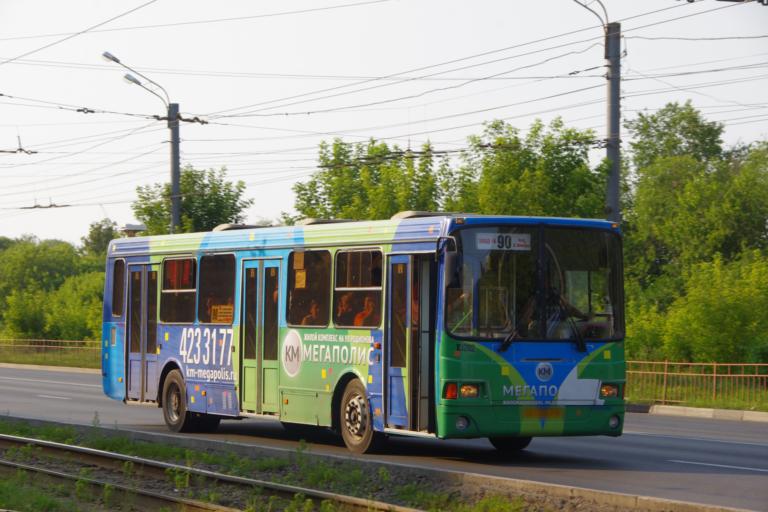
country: RU
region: Nizjnij Novgorod
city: Nizhniy Novgorod
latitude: 56.3383
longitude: 43.8825
